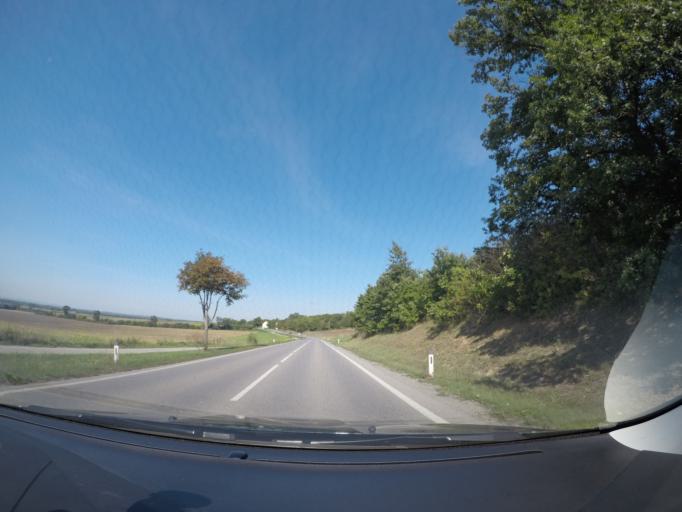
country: AT
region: Lower Austria
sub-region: Politischer Bezirk Bruck an der Leitha
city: Hof am Leithaberge
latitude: 47.9538
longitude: 16.5859
